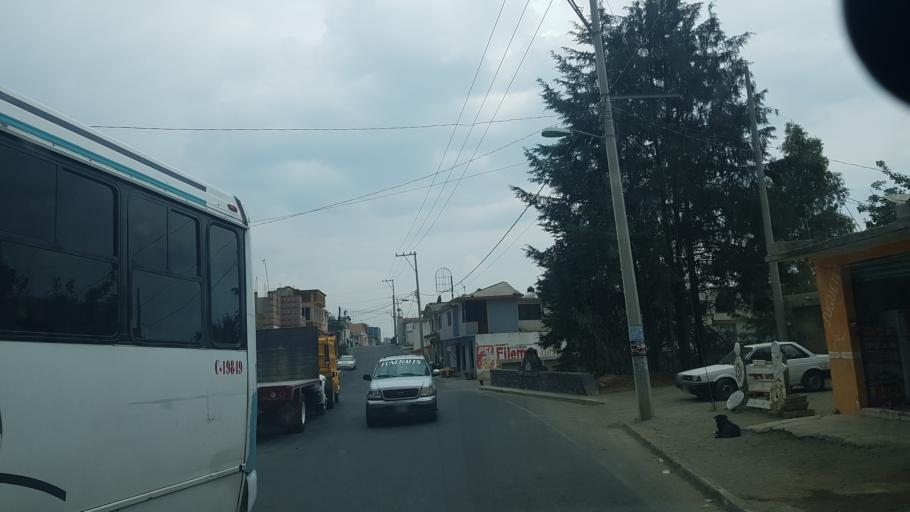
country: MX
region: Puebla
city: San Lorenzo Chiautzingo
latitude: 19.2002
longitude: -98.4609
